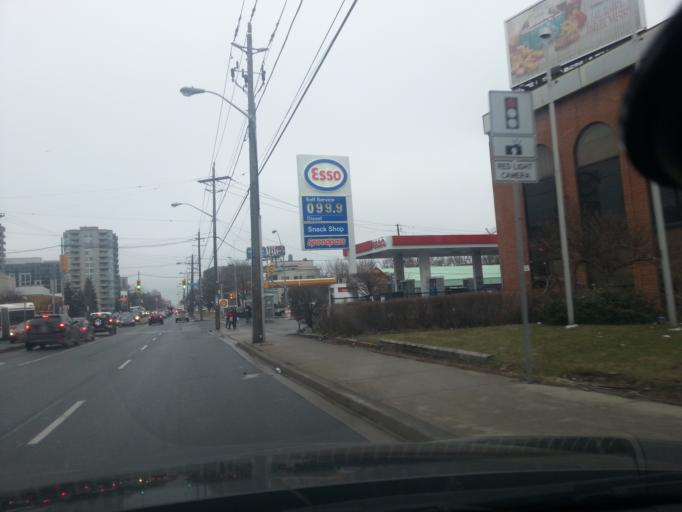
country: CA
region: Ontario
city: Toronto
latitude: 43.7187
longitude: -79.4295
